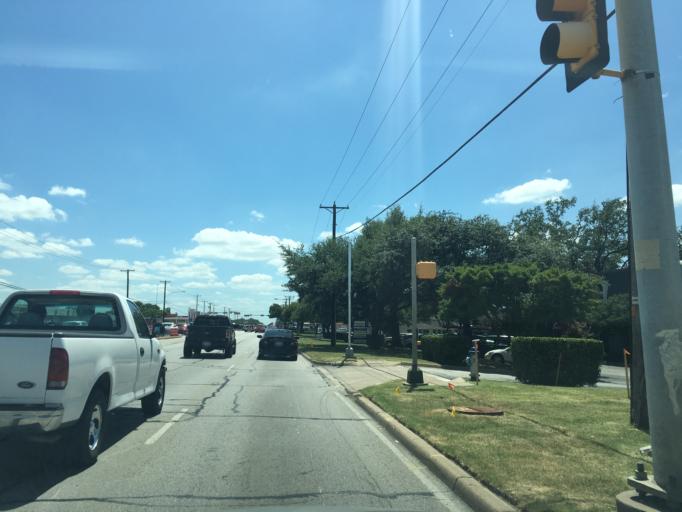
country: US
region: Texas
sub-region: Dallas County
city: Garland
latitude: 32.8447
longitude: -96.6894
